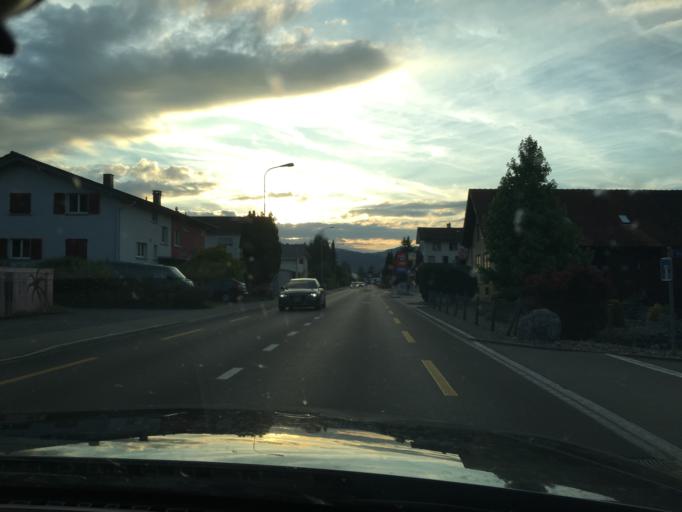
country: CH
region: Saint Gallen
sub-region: Wahlkreis Rheintal
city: Diepoldsau
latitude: 47.3809
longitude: 9.6646
